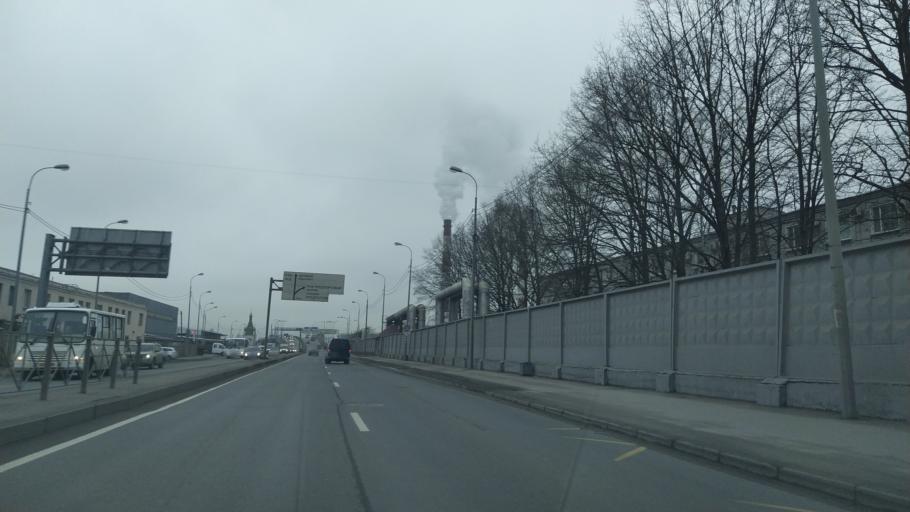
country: RU
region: St.-Petersburg
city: Dachnoye
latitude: 59.8324
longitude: 30.3037
